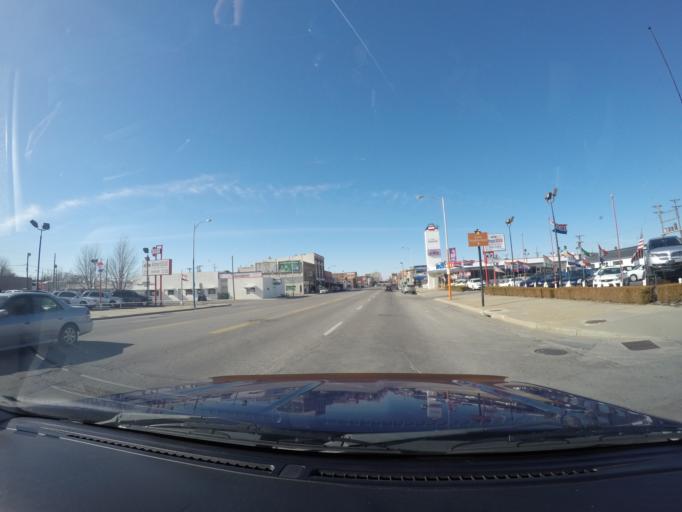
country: US
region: Kansas
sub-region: Sedgwick County
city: Wichita
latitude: 37.6862
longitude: -97.3220
